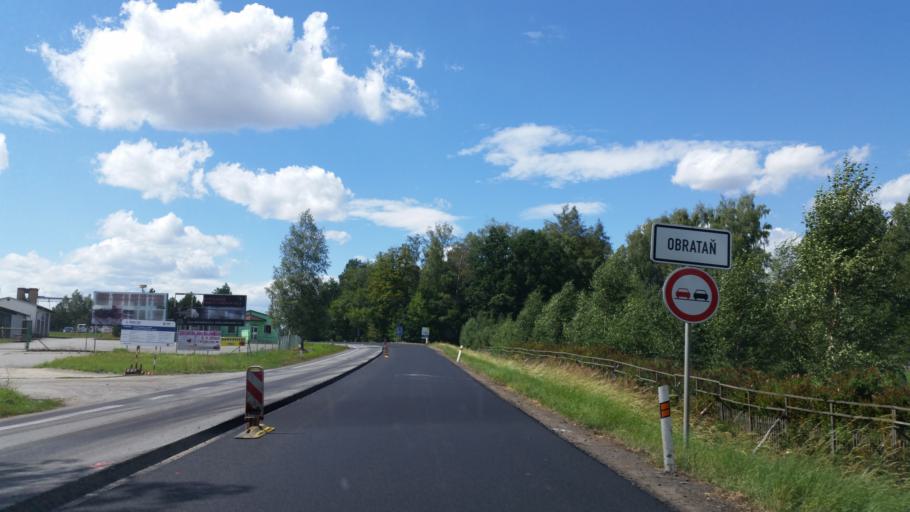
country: CZ
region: Vysocina
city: Cernovice
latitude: 49.4238
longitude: 14.9570
